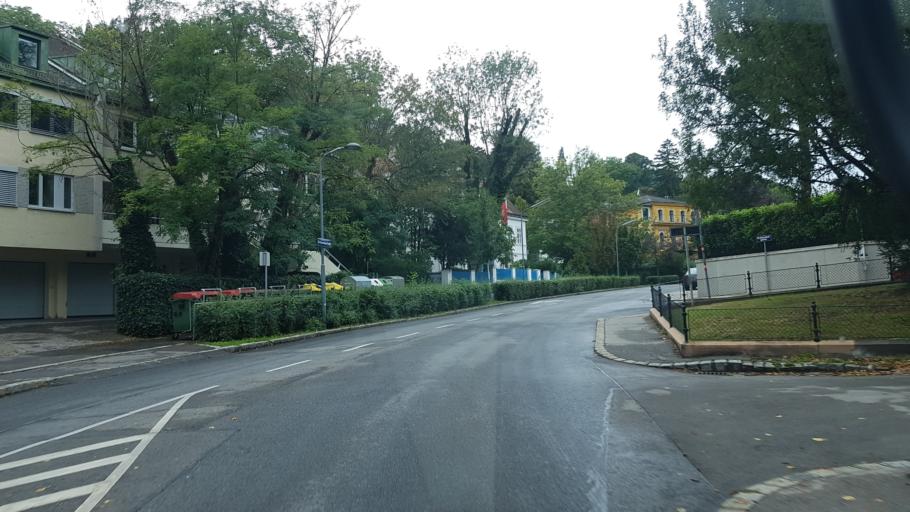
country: AT
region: Lower Austria
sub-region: Politischer Bezirk Wien-Umgebung
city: Klosterneuburg
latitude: 48.2519
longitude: 16.3209
